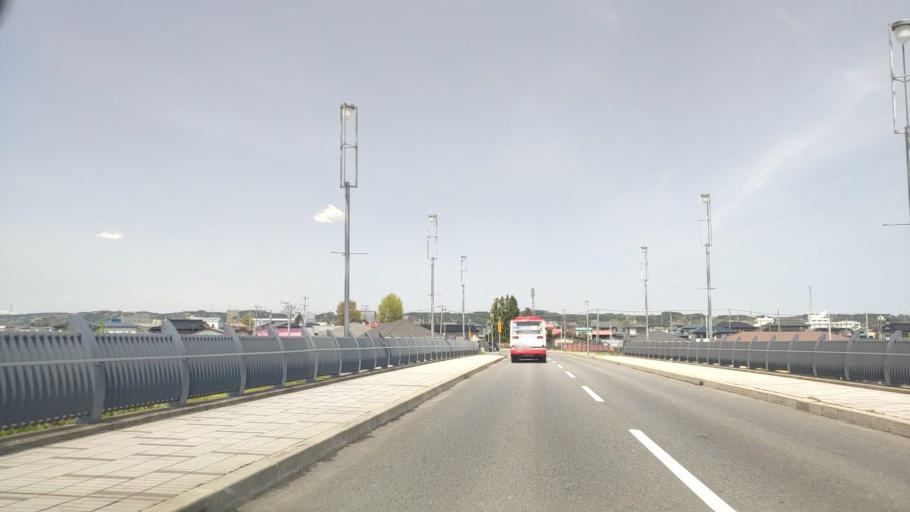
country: JP
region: Aomori
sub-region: Hachinohe Shi
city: Uchimaru
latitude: 40.5016
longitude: 141.4427
